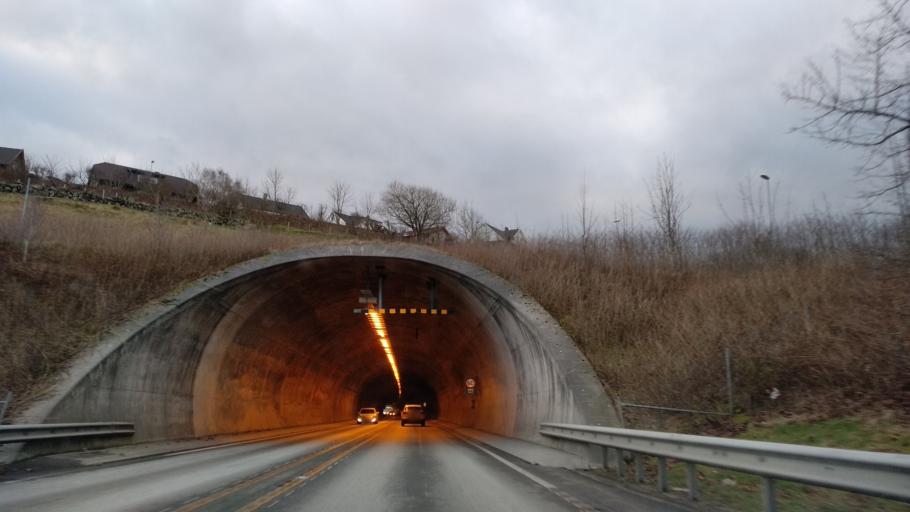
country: NO
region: Rogaland
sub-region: Klepp
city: Kleppe
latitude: 58.7781
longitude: 5.6227
